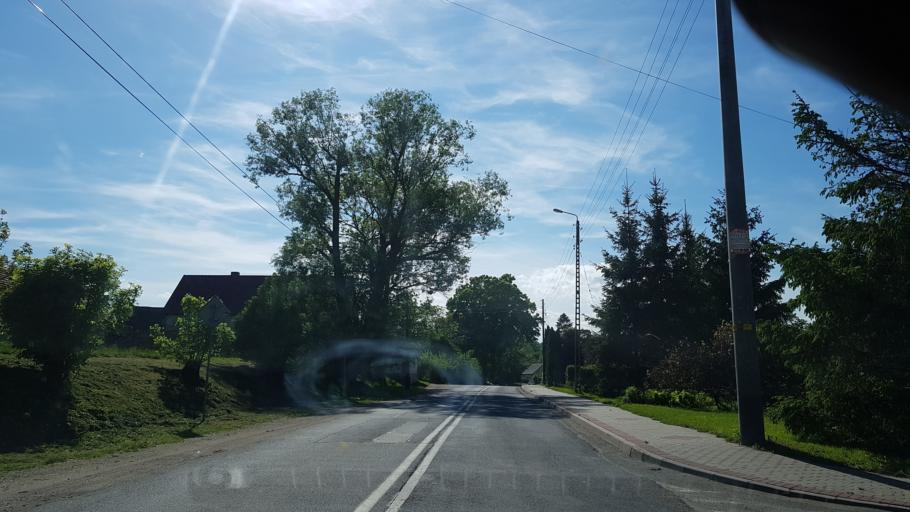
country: PL
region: Lower Silesian Voivodeship
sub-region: Powiat zabkowicki
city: Stoszowice
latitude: 50.5996
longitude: 16.7384
